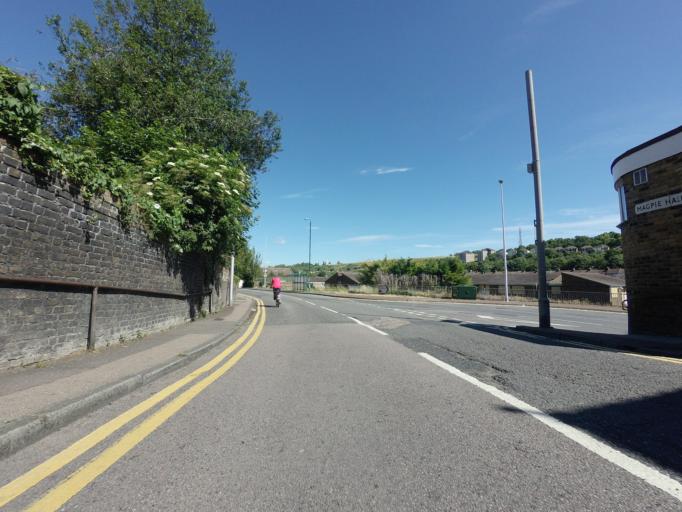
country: GB
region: England
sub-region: Kent
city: Chatham
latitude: 51.3754
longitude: 0.5350
